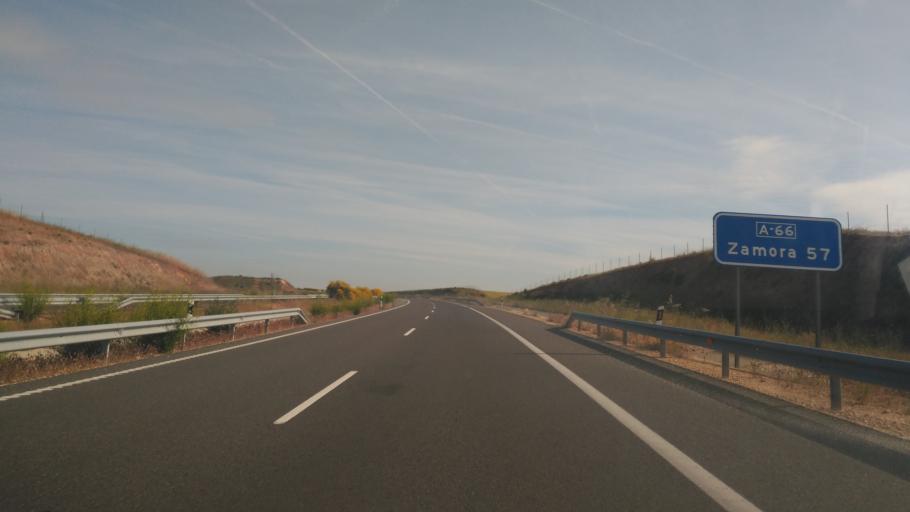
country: ES
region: Castille and Leon
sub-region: Provincia de Salamanca
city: Monterrubio de Armuna
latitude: 41.0418
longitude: -5.6670
